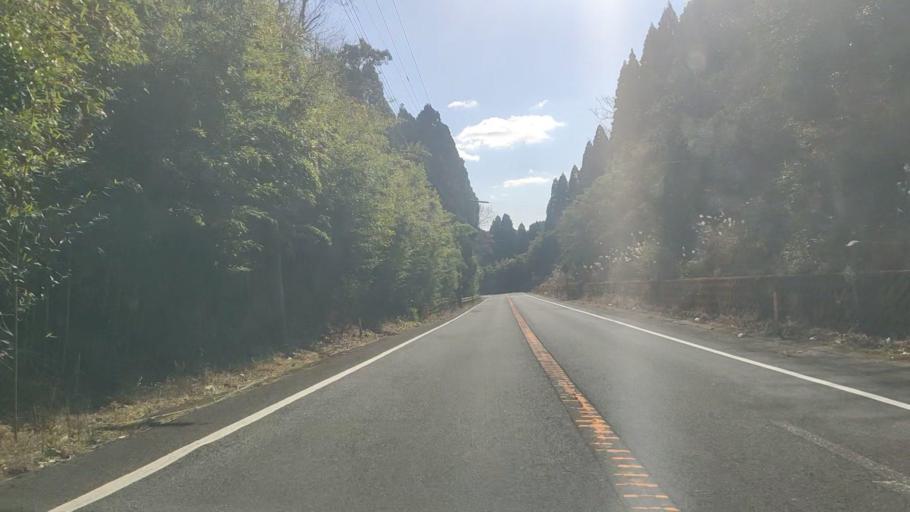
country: JP
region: Kagoshima
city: Kokubu-matsuki
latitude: 31.6655
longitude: 130.8808
